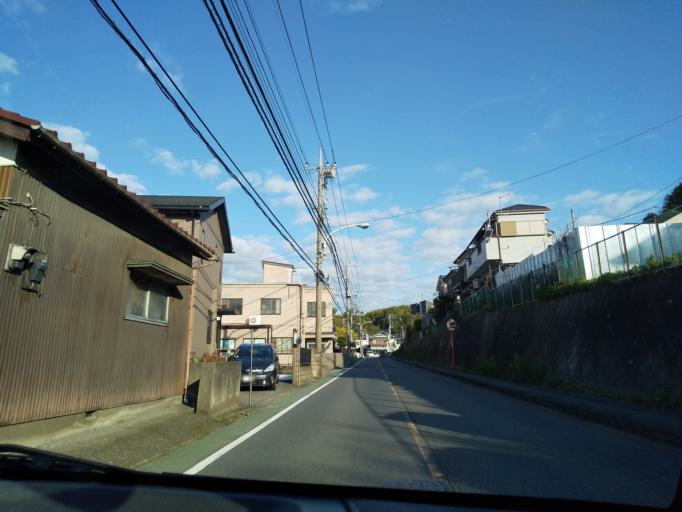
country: JP
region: Tokyo
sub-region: Machida-shi
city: Machida
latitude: 35.5945
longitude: 139.4549
